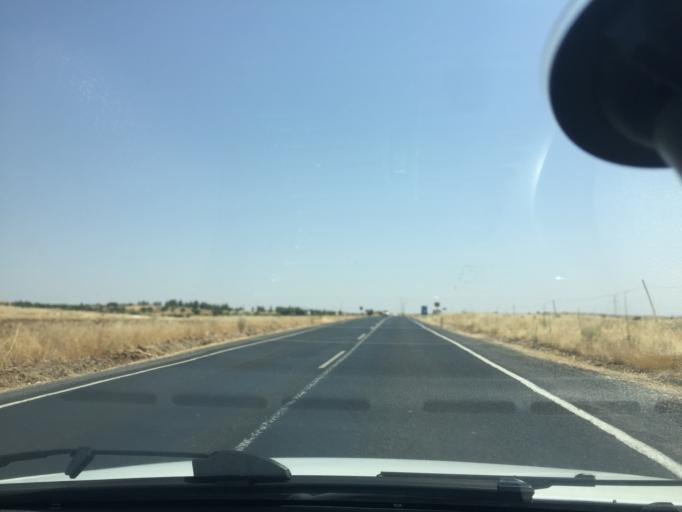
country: TR
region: Mardin
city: Acirli
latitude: 37.4418
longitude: 41.2902
